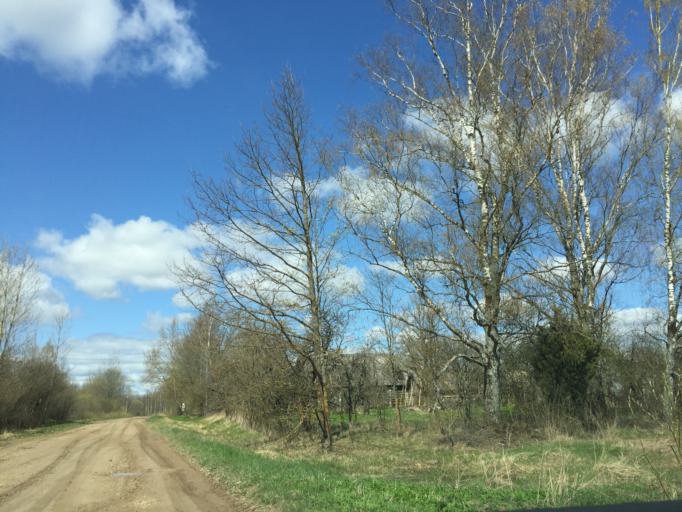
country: LV
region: Vilanu
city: Vilani
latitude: 56.6713
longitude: 27.0959
